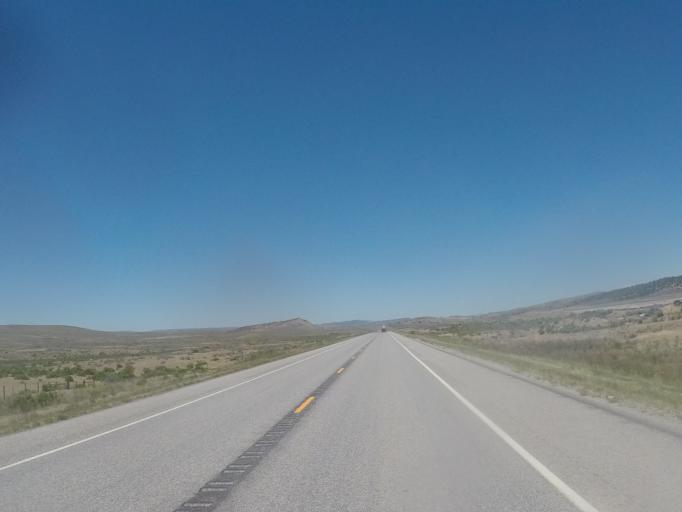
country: US
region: Montana
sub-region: Carbon County
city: Red Lodge
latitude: 45.1802
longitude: -108.8443
